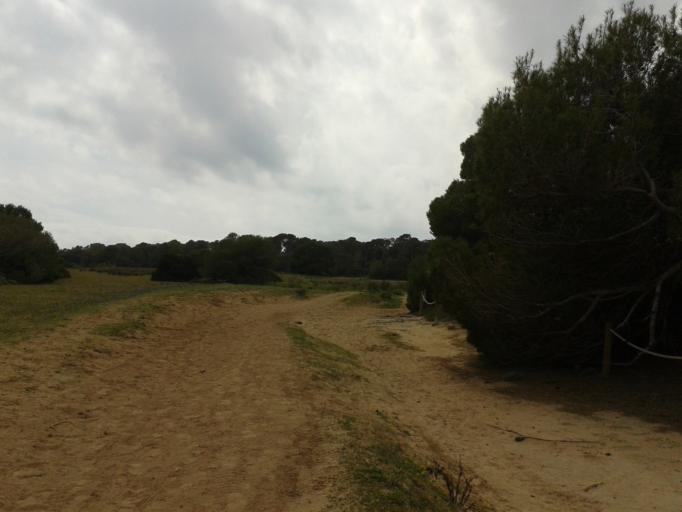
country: ES
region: Balearic Islands
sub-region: Illes Balears
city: Son Servera
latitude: 39.5845
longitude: 3.3908
